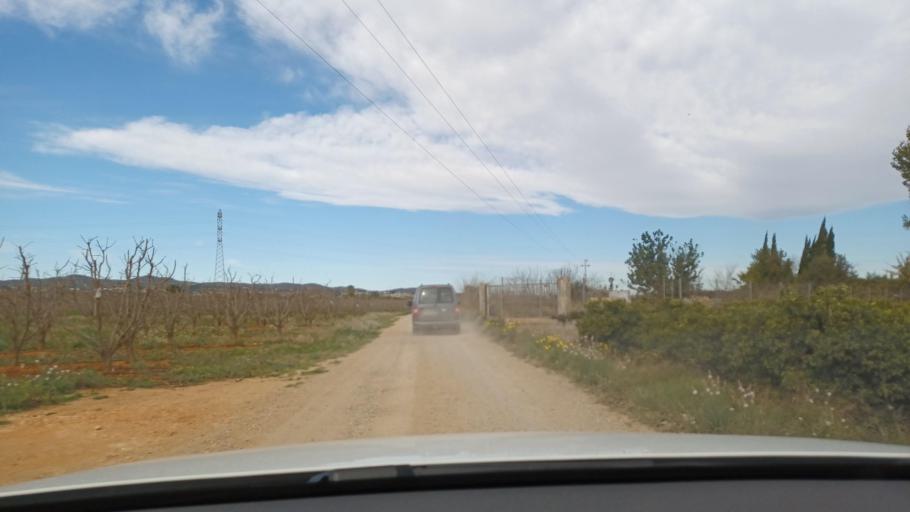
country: ES
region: Valencia
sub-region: Provincia de Valencia
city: Benifaio
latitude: 39.2913
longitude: -0.4425
